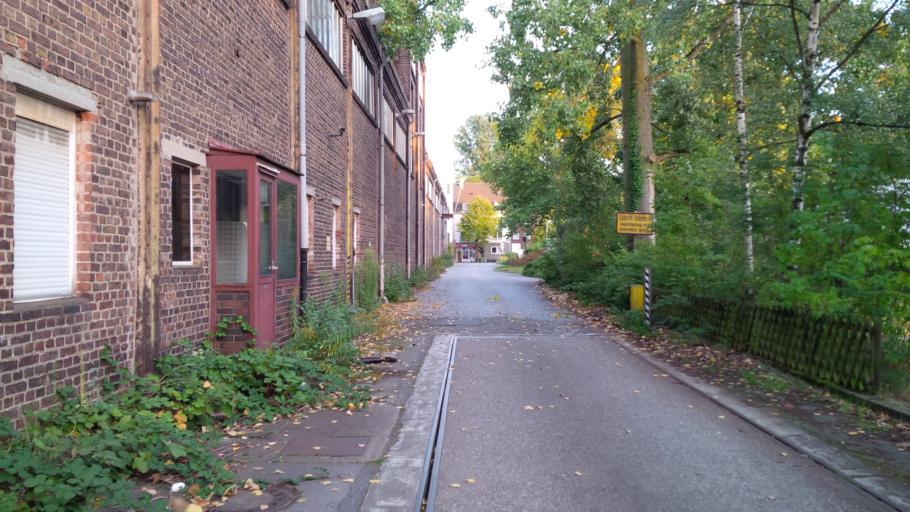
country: DE
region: North Rhine-Westphalia
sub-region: Regierungsbezirk Dusseldorf
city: Oberhausen
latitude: 51.4727
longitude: 6.8265
